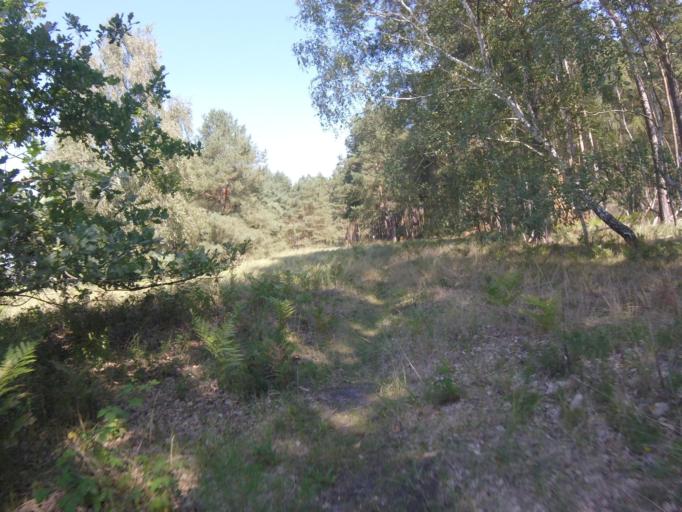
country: DE
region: Brandenburg
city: Mittenwalde
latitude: 52.2256
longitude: 13.5884
